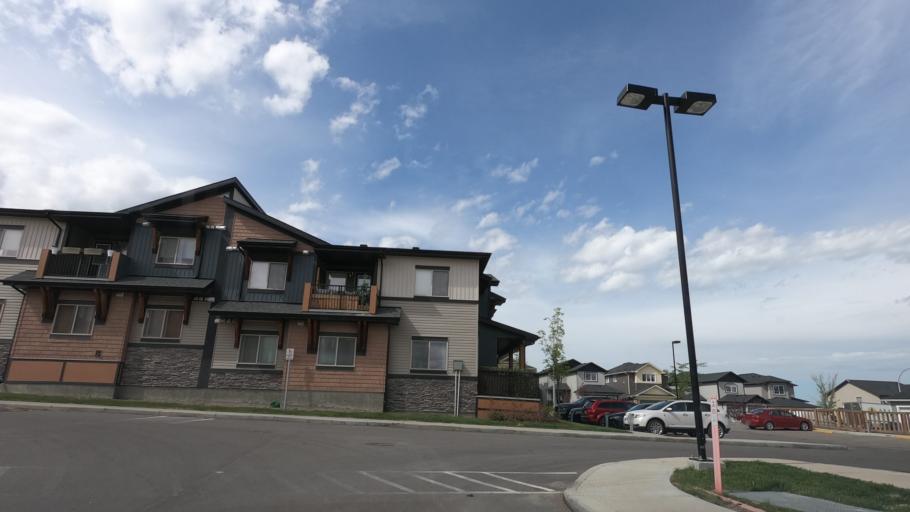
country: CA
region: Alberta
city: Airdrie
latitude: 51.2742
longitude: -114.0472
